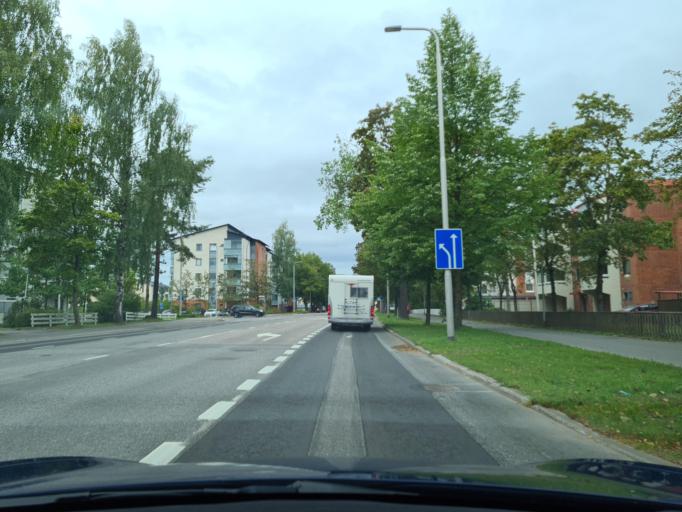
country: FI
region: South Karelia
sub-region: Lappeenranta
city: Lappeenranta
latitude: 61.0526
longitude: 28.1853
